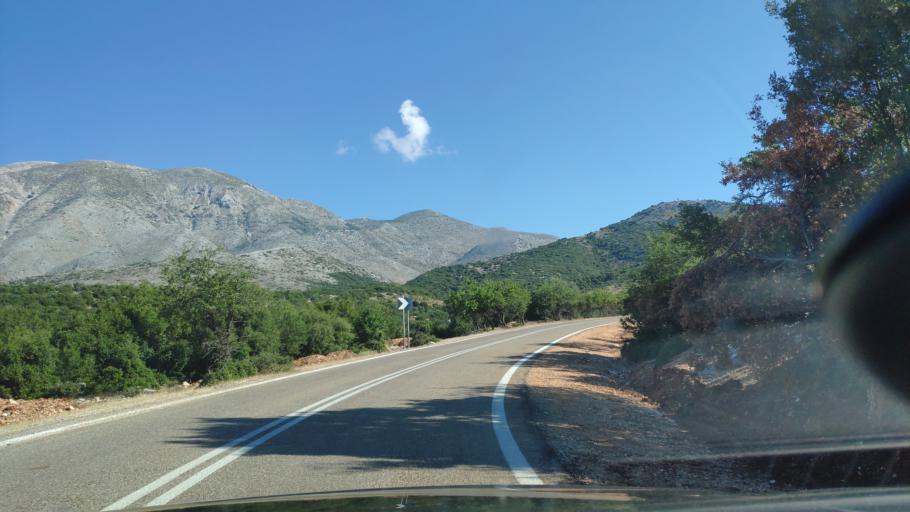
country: GR
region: West Greece
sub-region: Nomos Aitolias kai Akarnanias
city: Archontochorion
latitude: 38.6888
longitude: 21.0592
